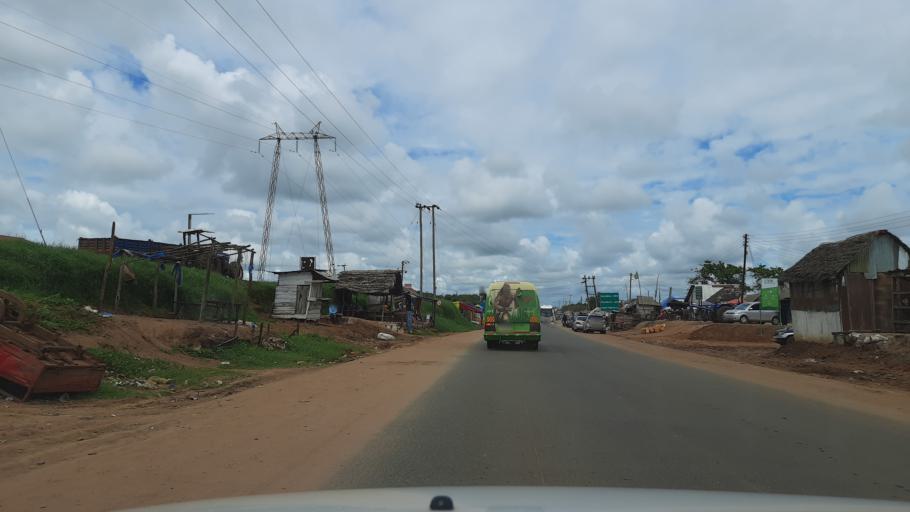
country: TZ
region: Tanga
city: Chanika
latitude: -5.7872
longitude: 38.2907
